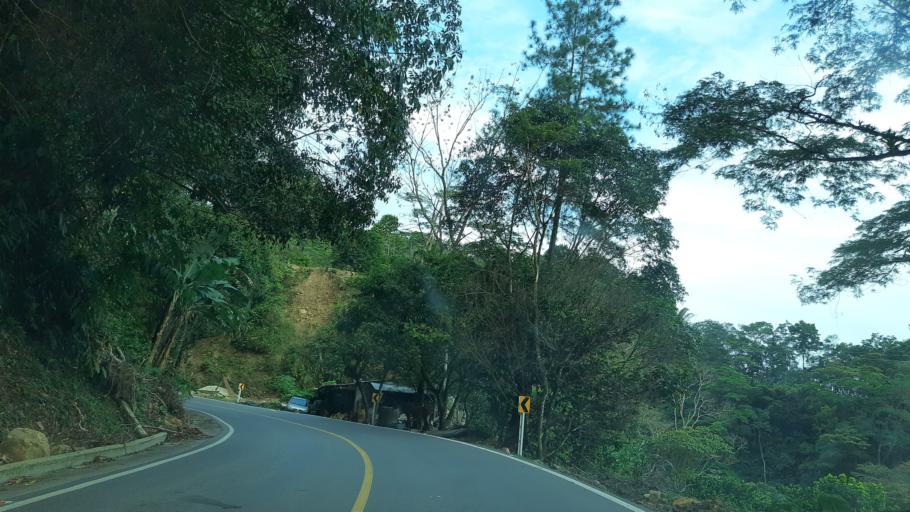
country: CO
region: Boyaca
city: San Luis de Gaceno
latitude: 4.8347
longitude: -73.2090
